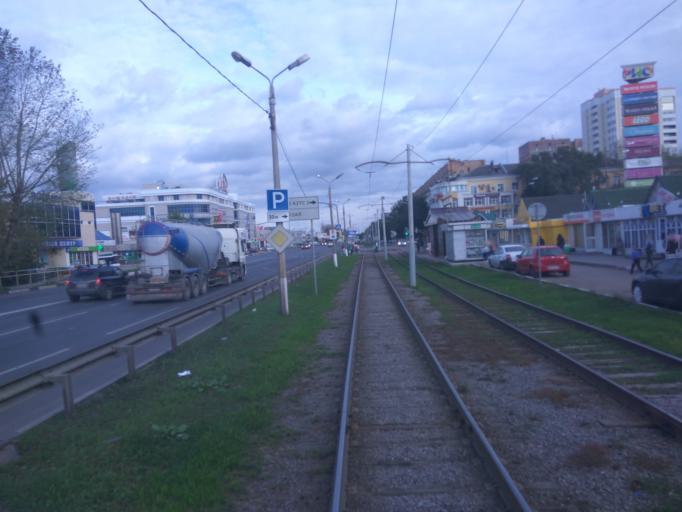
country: RU
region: Moskovskaya
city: Kolomna
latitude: 55.0844
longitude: 38.8017
